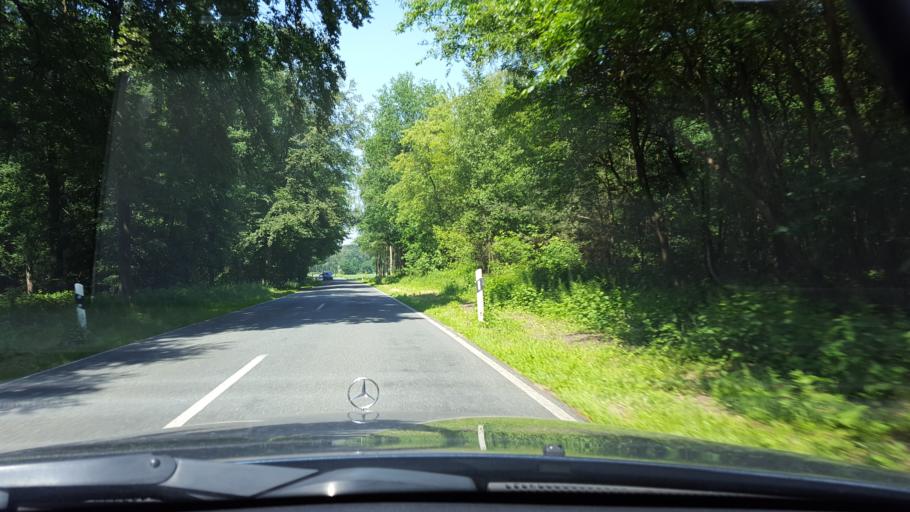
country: DE
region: North Rhine-Westphalia
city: Olfen
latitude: 51.7186
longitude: 7.3066
